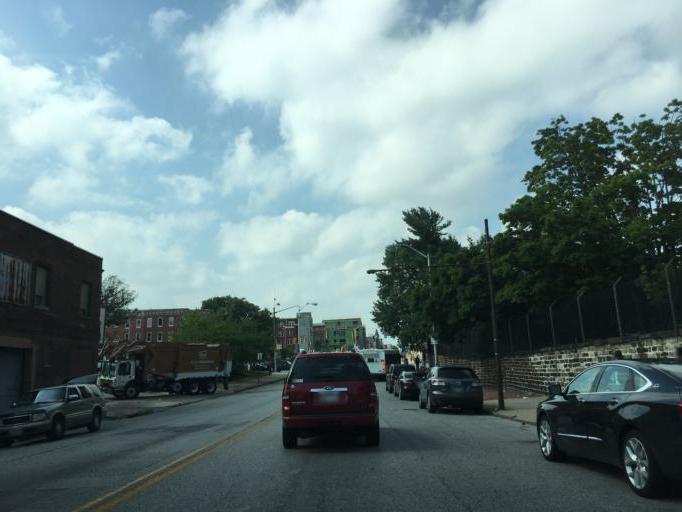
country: US
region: Maryland
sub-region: City of Baltimore
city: Baltimore
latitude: 39.3105
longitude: -76.6094
